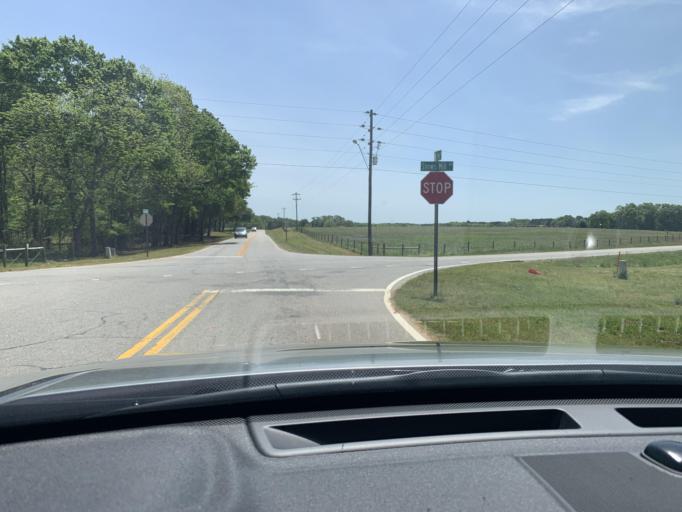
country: US
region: Georgia
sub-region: Oconee County
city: Bogart
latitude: 33.8564
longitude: -83.5486
